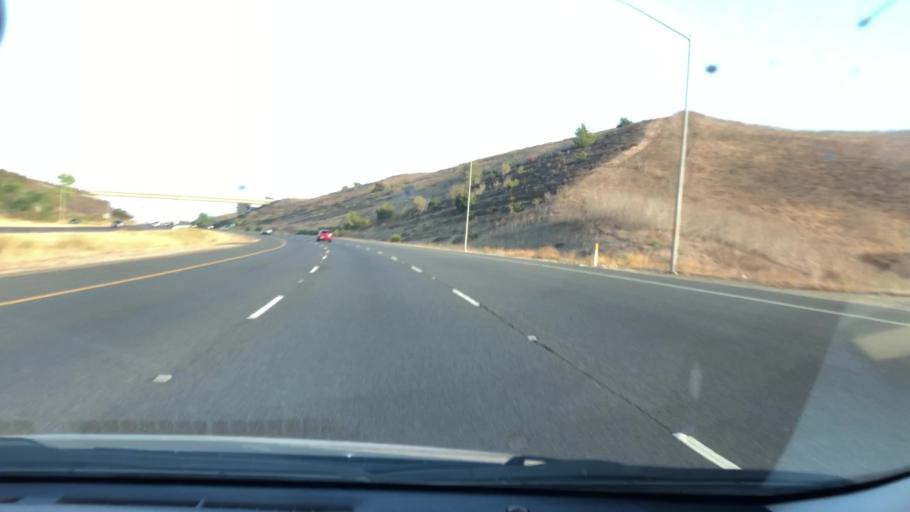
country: US
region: California
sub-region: Orange County
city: North Tustin
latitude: 33.7749
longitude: -117.7461
